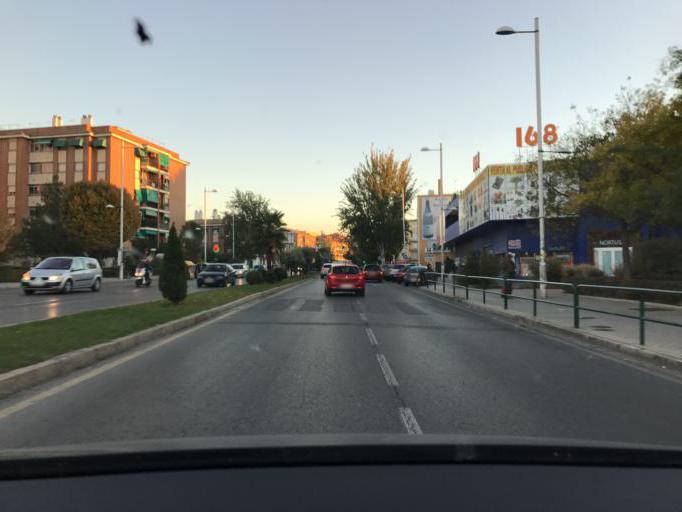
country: ES
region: Andalusia
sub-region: Provincia de Granada
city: Granada
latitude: 37.1966
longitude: -3.6101
